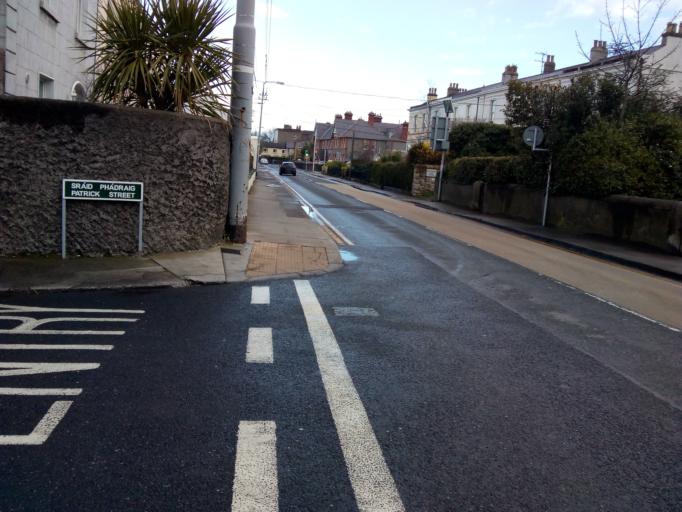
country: IE
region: Leinster
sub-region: Dun Laoghaire-Rathdown
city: Dun Laoghaire
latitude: 53.2880
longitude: -6.1386
